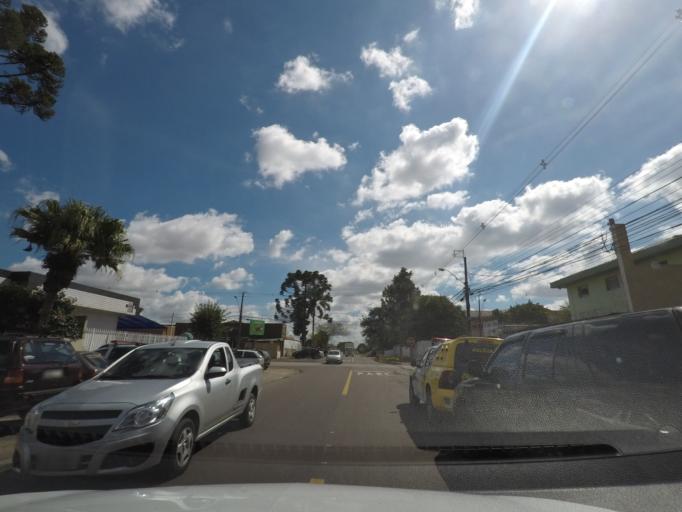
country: BR
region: Parana
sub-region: Sao Jose Dos Pinhais
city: Sao Jose dos Pinhais
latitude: -25.5007
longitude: -49.2353
